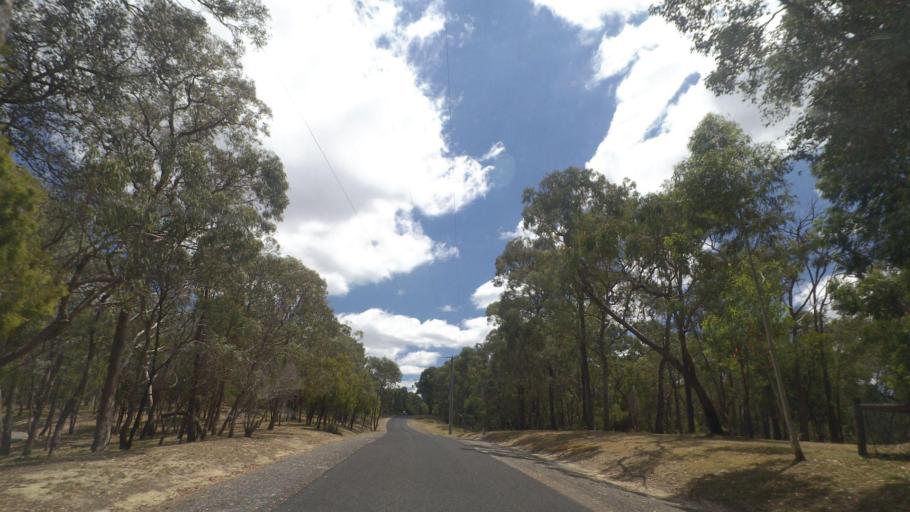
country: AU
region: Victoria
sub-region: Manningham
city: Warrandyte
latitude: -37.7319
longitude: 145.2594
